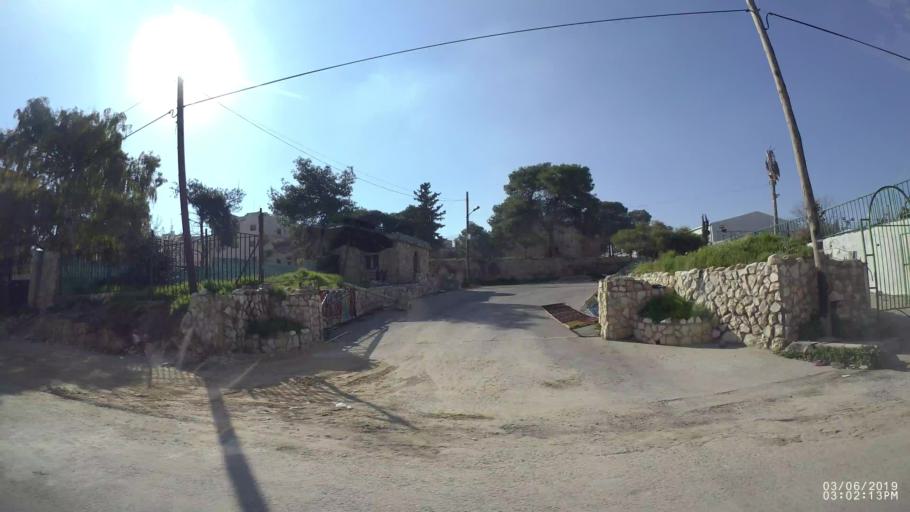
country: JO
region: Amman
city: Amman
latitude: 31.9882
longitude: 35.9434
